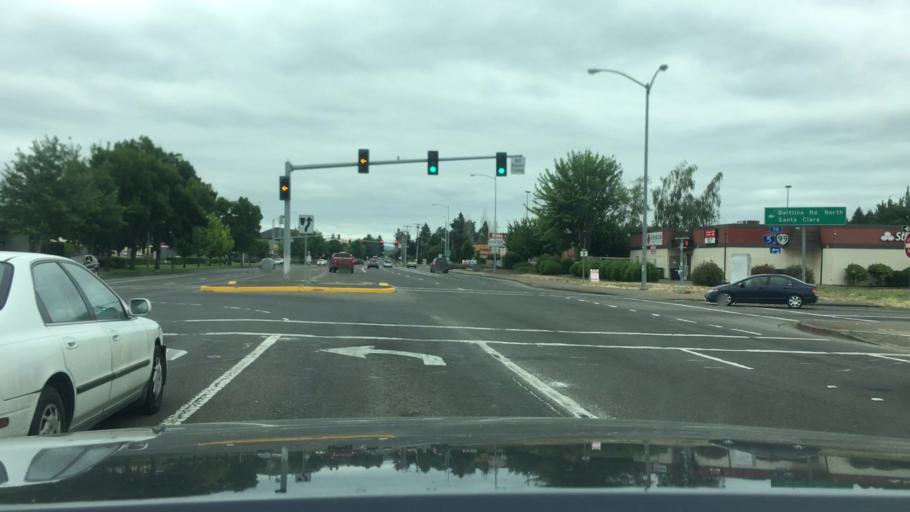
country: US
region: Oregon
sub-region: Lane County
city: Eugene
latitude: 44.0845
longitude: -123.1710
